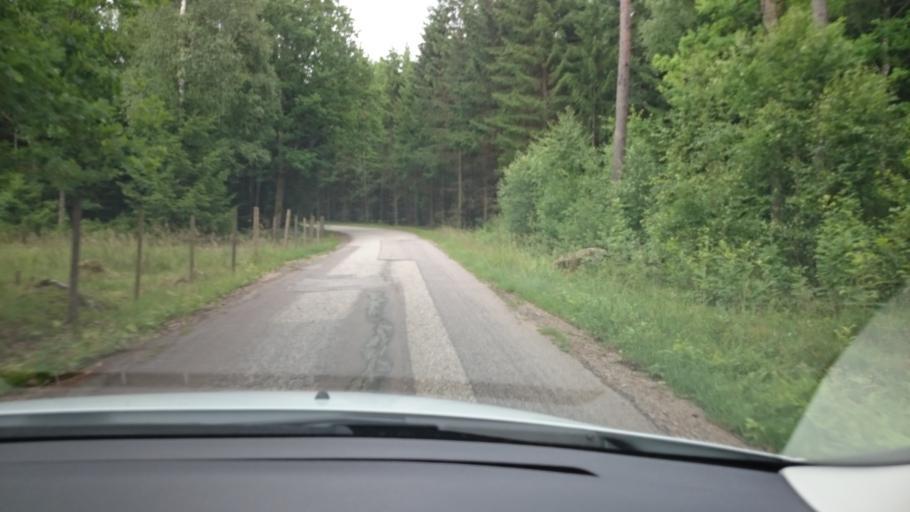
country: SE
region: Halland
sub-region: Hylte Kommun
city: Hyltebruk
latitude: 56.9812
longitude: 13.2194
